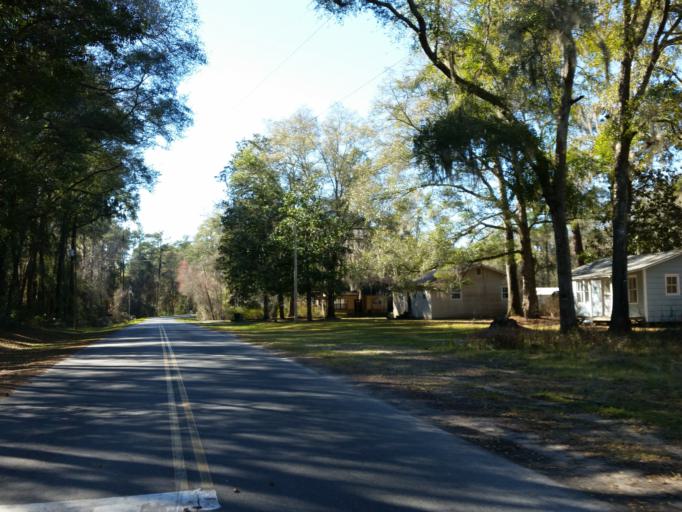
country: US
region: Florida
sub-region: Suwannee County
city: Wellborn
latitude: 30.3345
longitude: -82.7654
